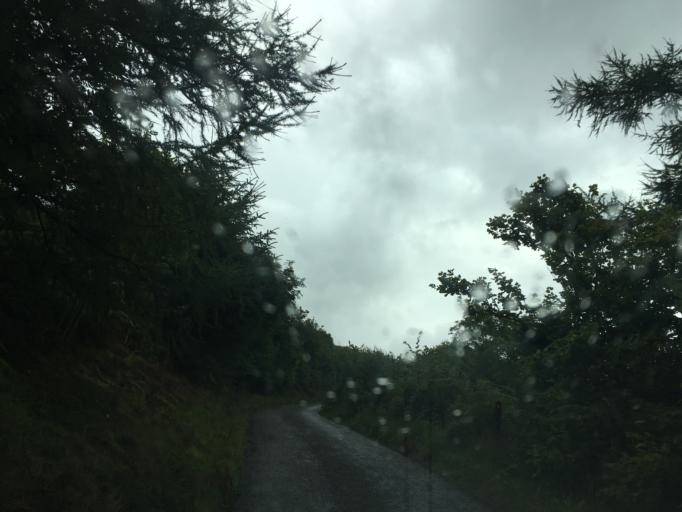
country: GB
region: Scotland
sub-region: Argyll and Bute
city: Oban
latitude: 56.2597
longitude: -5.4660
